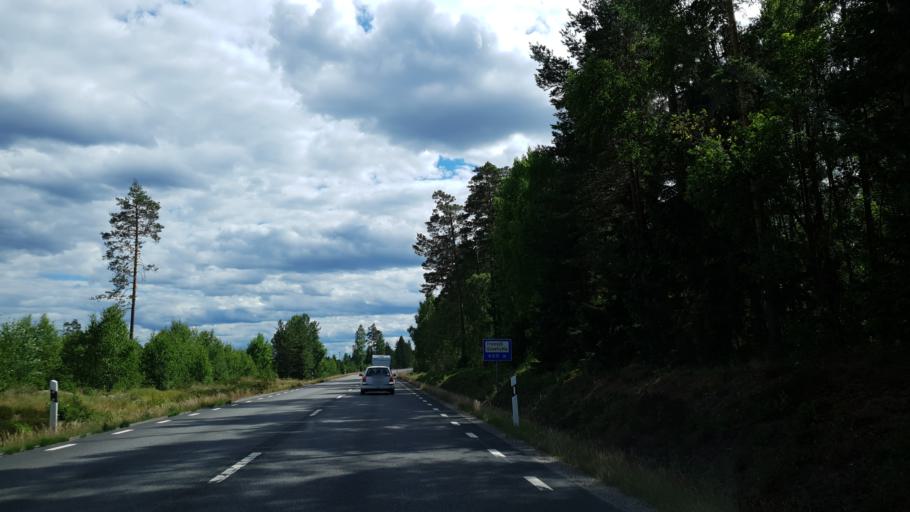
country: SE
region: Kronoberg
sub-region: Lessebo Kommun
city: Lessebo
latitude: 56.8061
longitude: 15.4122
